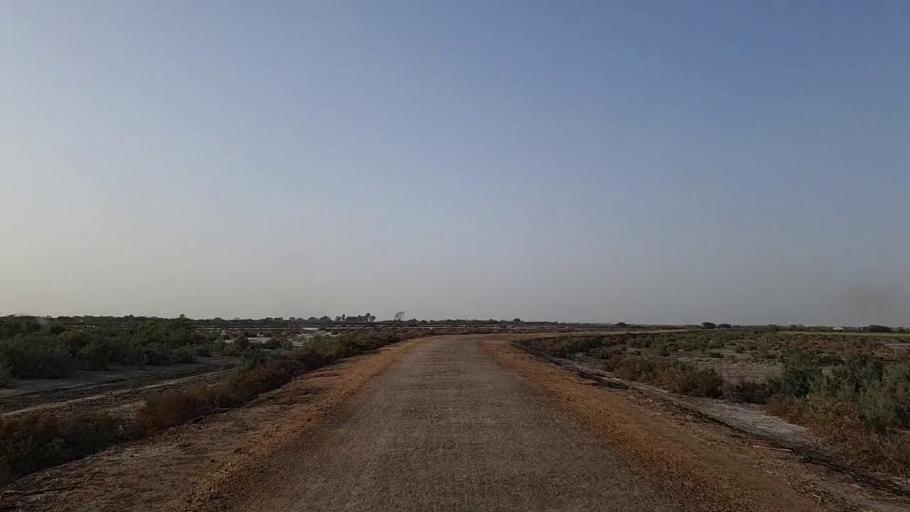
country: PK
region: Sindh
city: Jati
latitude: 24.3630
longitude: 68.1453
